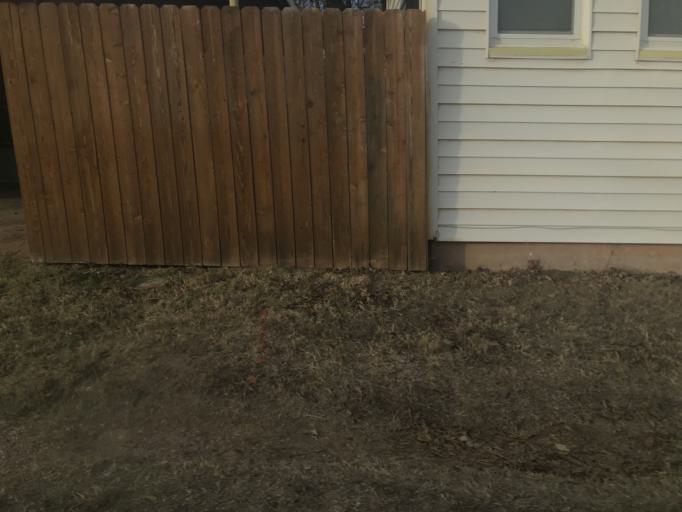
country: US
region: Texas
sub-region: Taylor County
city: Abilene
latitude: 32.4322
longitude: -99.7472
